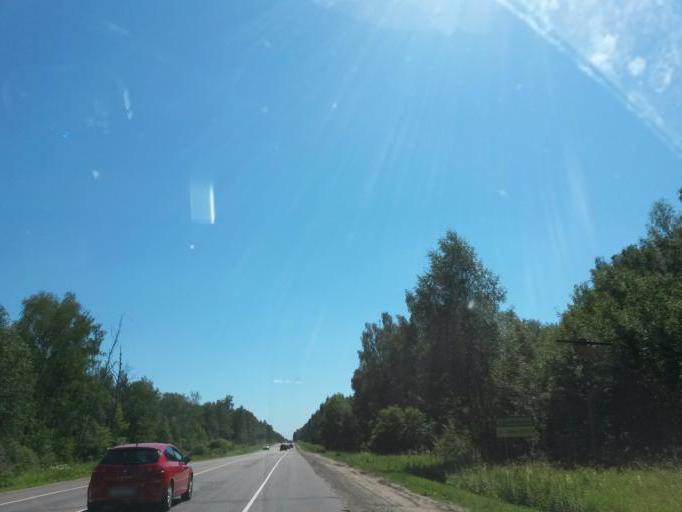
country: RU
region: Moskovskaya
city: Proletarskiy
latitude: 55.0597
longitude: 37.4348
